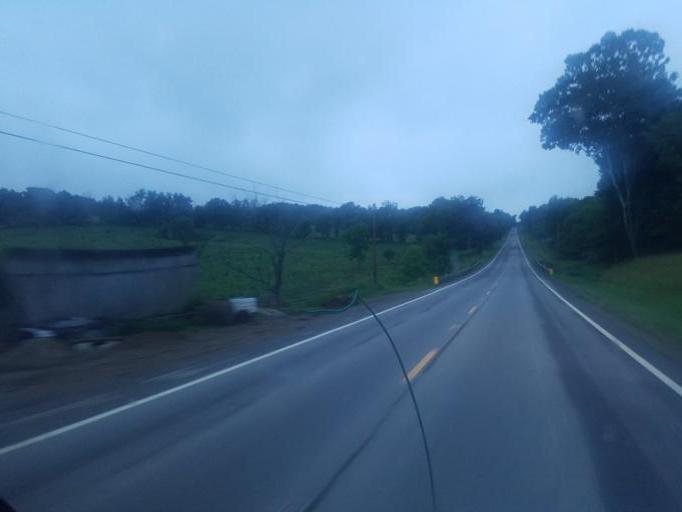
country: US
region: Ohio
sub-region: Carroll County
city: Carrollton
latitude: 40.5391
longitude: -81.0291
